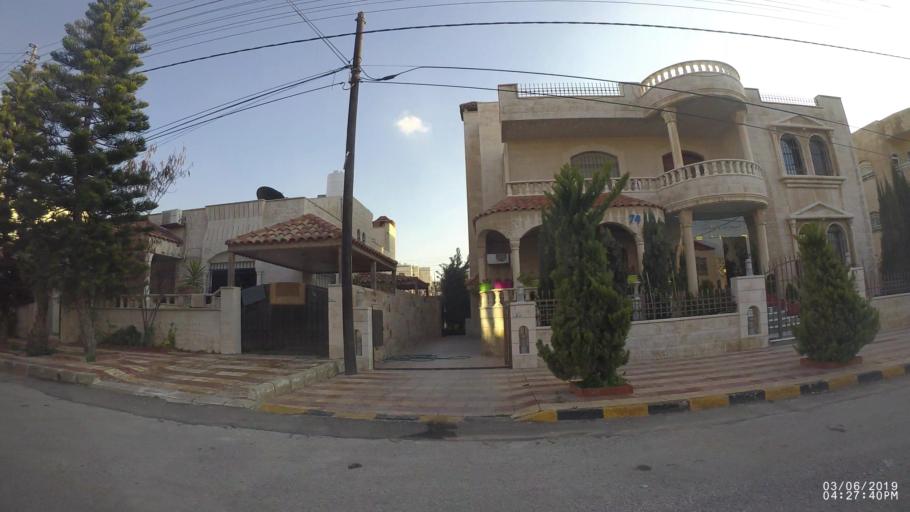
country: JO
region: Amman
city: Amman
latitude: 31.9859
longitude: 35.9611
